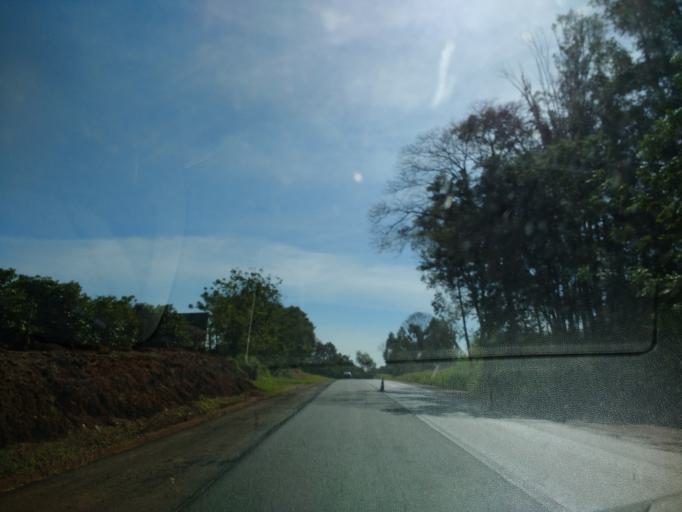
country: BR
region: Parana
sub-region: Umuarama
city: Umuarama
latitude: -23.8680
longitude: -53.3931
